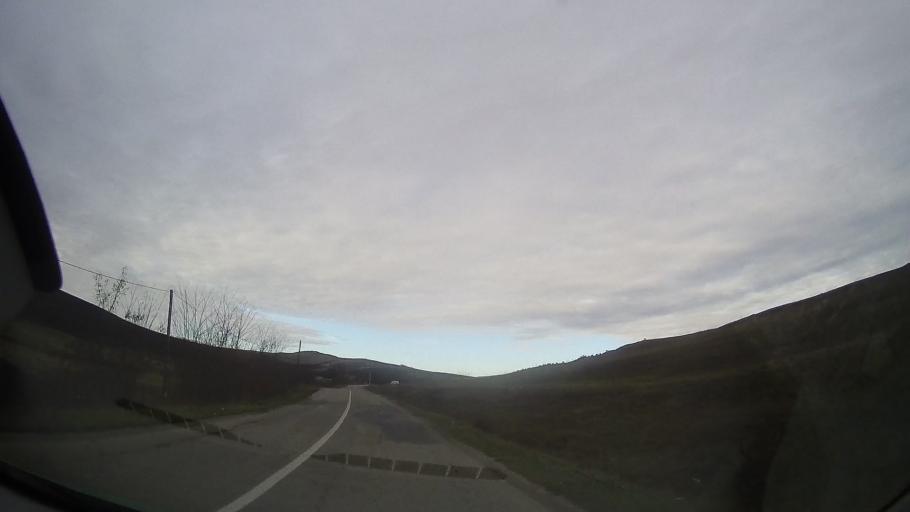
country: RO
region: Cluj
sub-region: Comuna Camarasu
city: Camarasu
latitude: 46.8125
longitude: 24.1430
